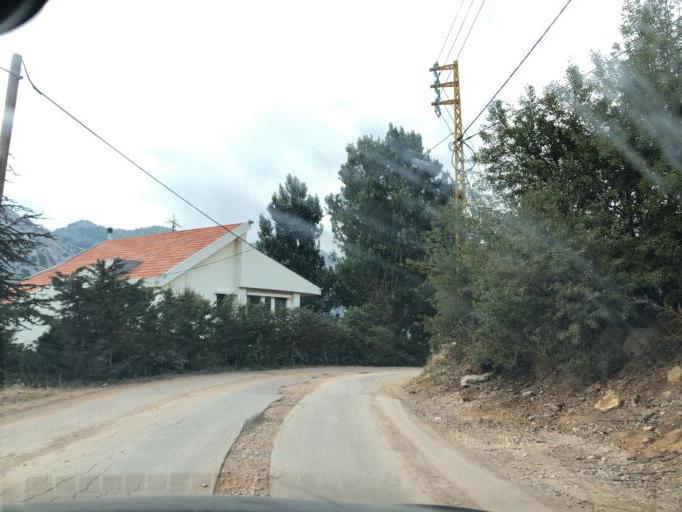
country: LB
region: Liban-Nord
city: Amioun
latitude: 34.1693
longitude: 35.8722
